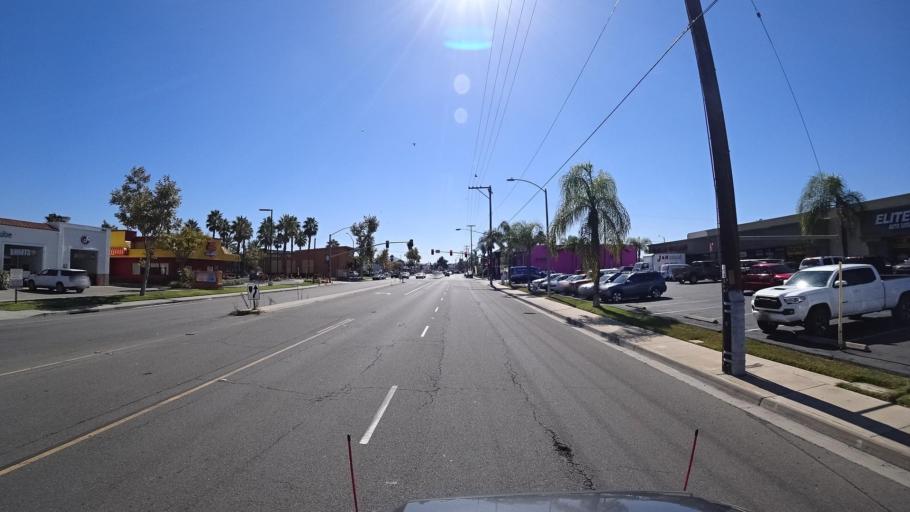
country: US
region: California
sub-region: San Diego County
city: Santee
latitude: 32.8212
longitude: -116.9624
